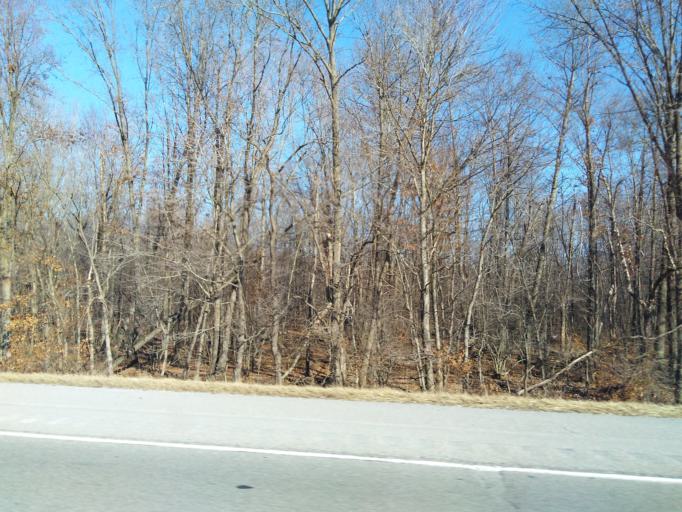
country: US
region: Illinois
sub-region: Williamson County
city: Johnston City
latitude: 37.8110
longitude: -88.9458
